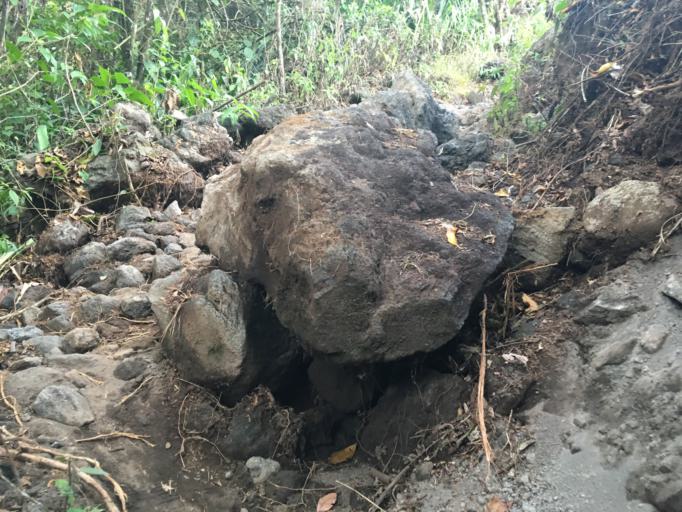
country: CR
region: Alajuela
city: La Fortuna
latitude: 10.4516
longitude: -84.7253
